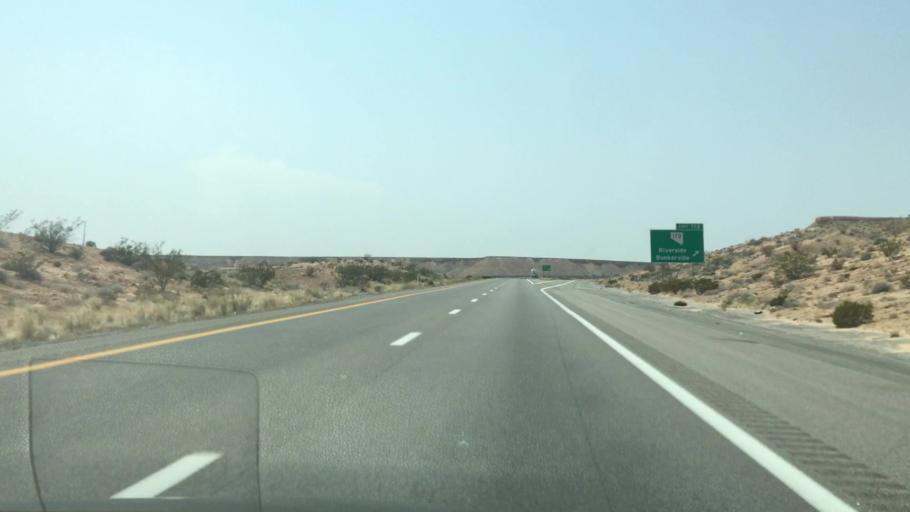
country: US
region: Nevada
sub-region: Clark County
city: Bunkerville
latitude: 36.7704
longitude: -114.2297
